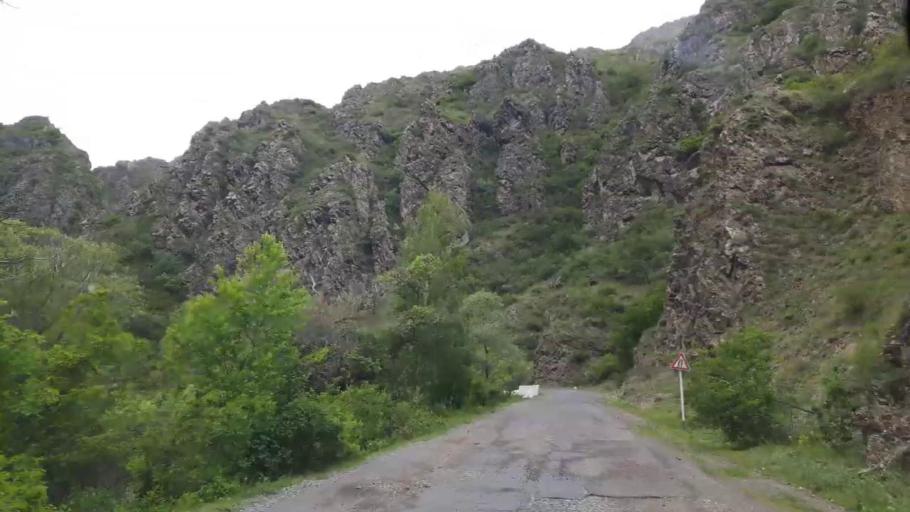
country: GE
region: Shida Kartli
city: Gori
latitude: 41.9002
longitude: 44.0661
